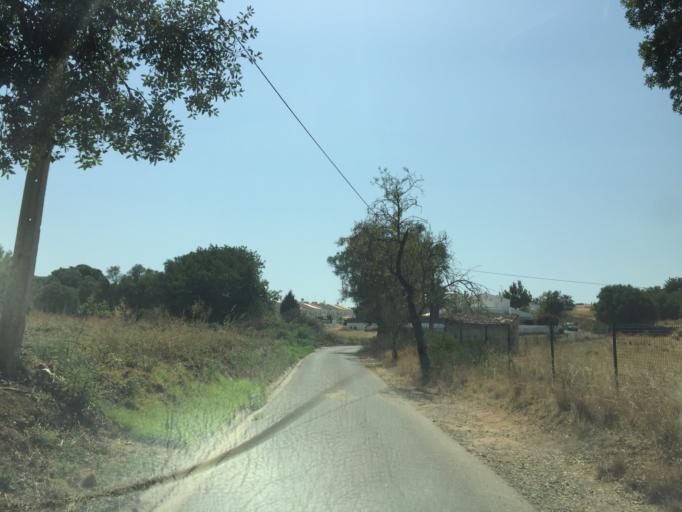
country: PT
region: Faro
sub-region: Loule
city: Boliqueime
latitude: 37.1081
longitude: -8.1944
